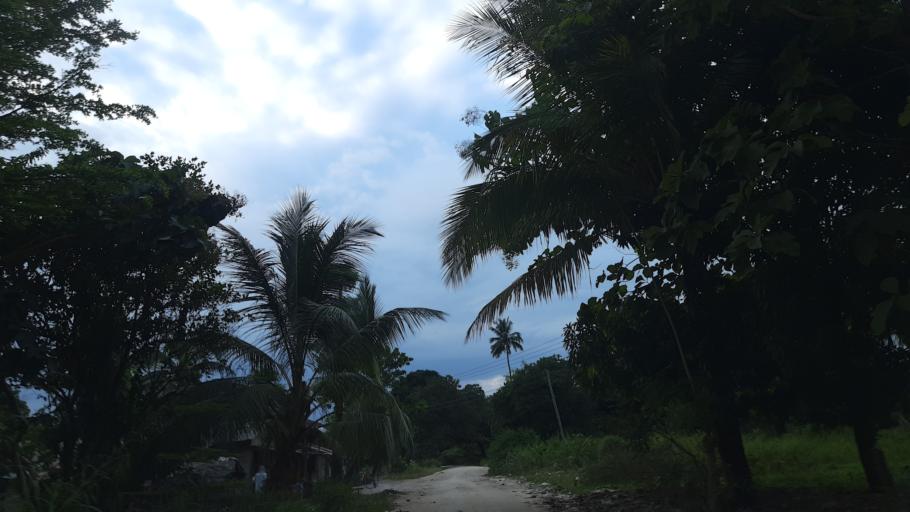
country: TZ
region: Pwani
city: Bagamoyo
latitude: -6.5156
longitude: 38.9295
